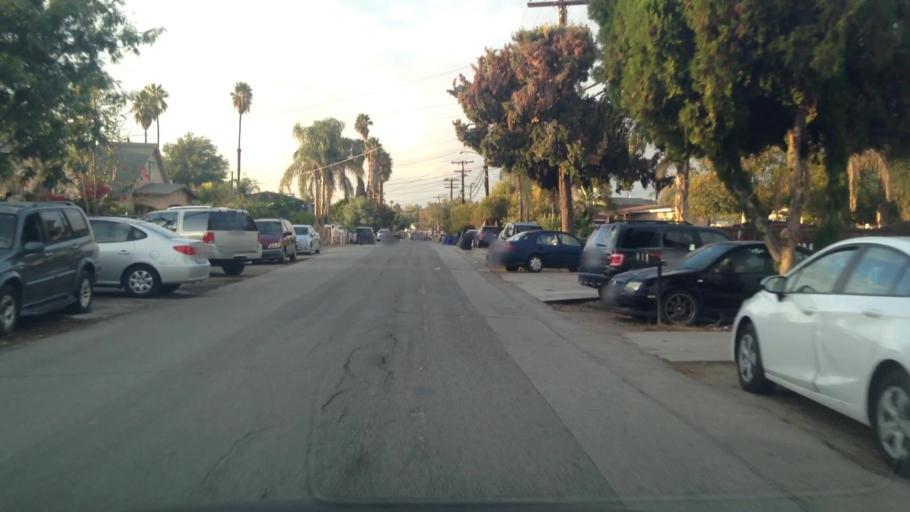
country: US
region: California
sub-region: Riverside County
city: Home Gardens
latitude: 33.9189
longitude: -117.4827
